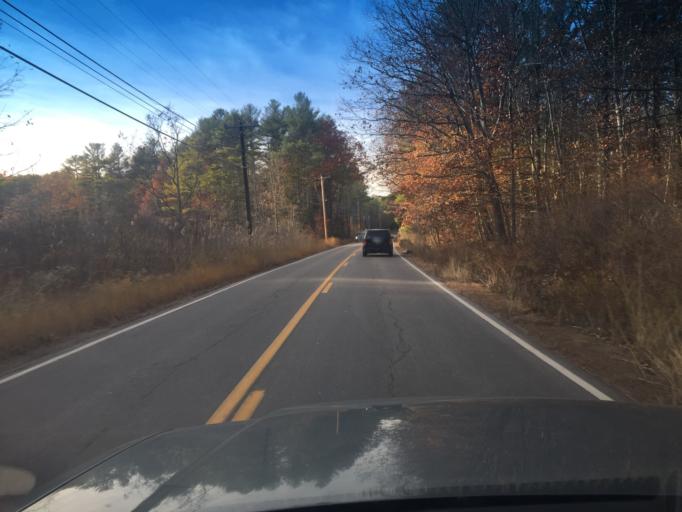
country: US
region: Maine
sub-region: York County
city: Eliot
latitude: 43.1738
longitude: -70.7201
